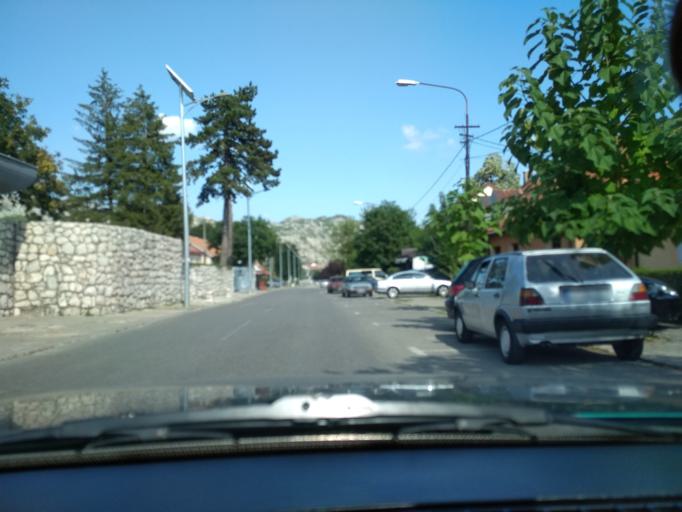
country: ME
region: Cetinje
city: Cetinje
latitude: 42.3932
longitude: 18.9117
